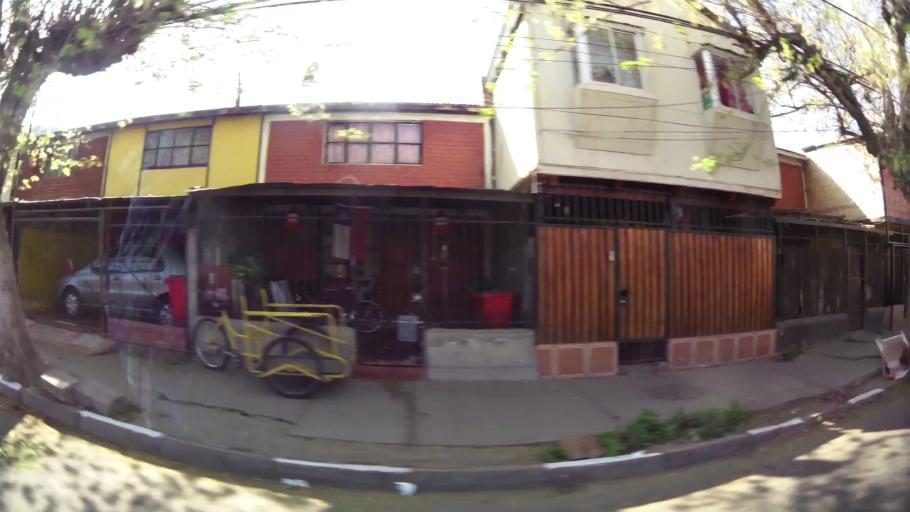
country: CL
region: Santiago Metropolitan
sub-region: Provincia de Santiago
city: Lo Prado
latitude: -33.4601
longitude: -70.7563
